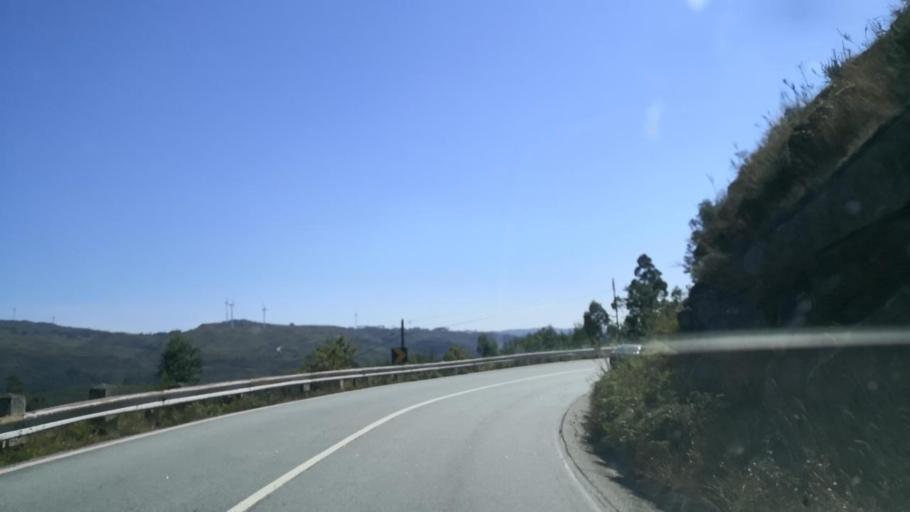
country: PT
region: Braga
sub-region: Fafe
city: Fafe
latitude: 41.4956
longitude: -8.0882
